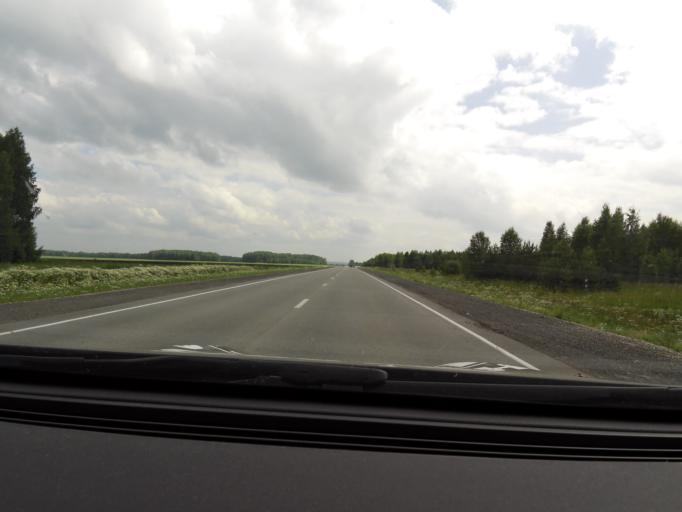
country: RU
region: Perm
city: Suksun
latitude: 56.9854
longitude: 57.5012
